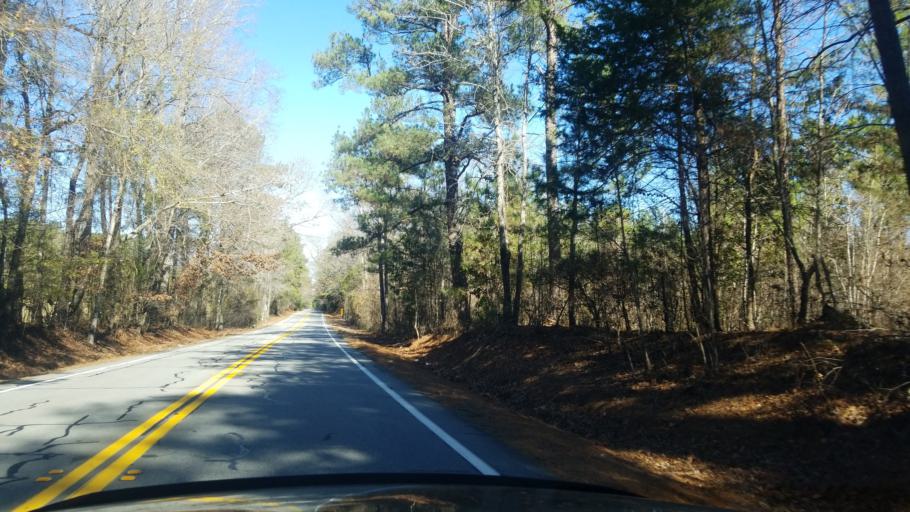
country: US
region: Georgia
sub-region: Harris County
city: Hamilton
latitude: 32.6772
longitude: -84.8591
